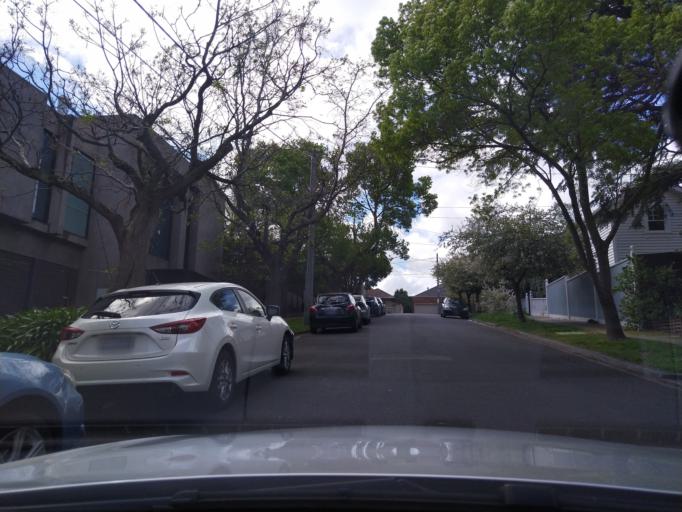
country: AU
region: Victoria
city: Rosanna
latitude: -37.7606
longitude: 145.0624
